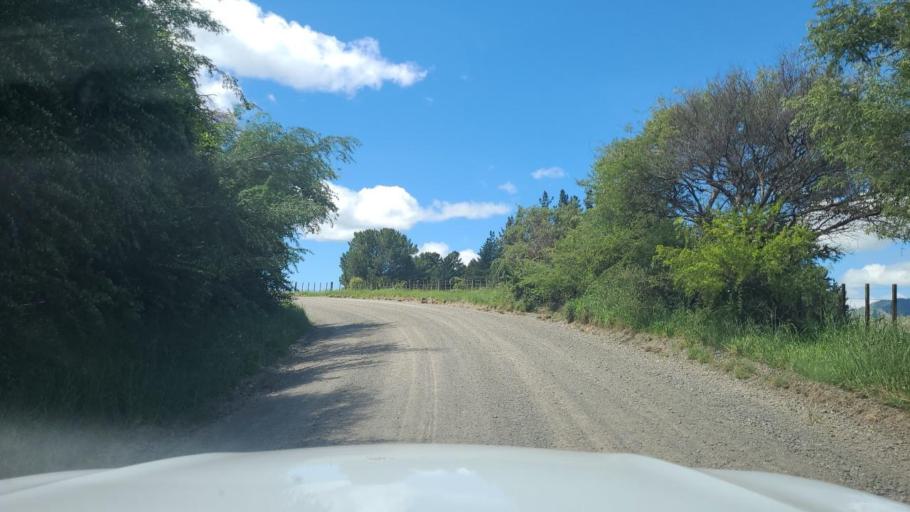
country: NZ
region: Hawke's Bay
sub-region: Napier City
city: Napier
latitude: -39.2165
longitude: 176.7517
